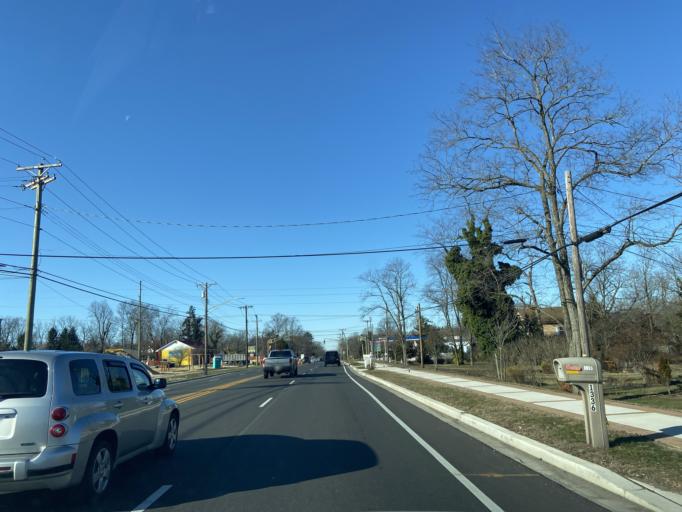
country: US
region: New Jersey
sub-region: Cumberland County
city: Vineland
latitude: 39.4875
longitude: -75.0510
